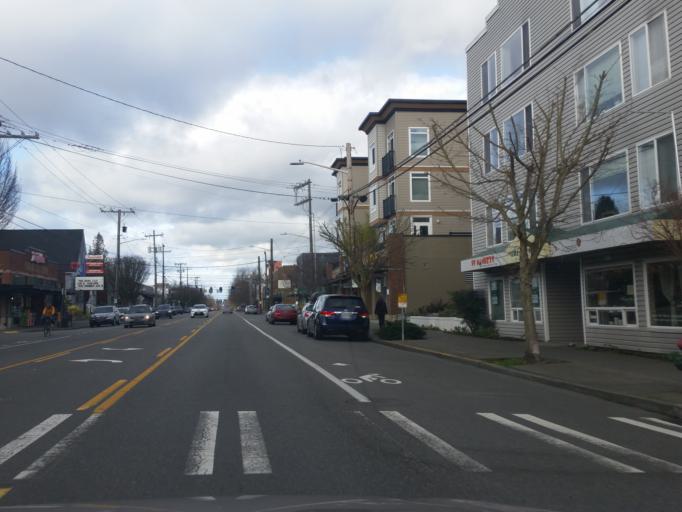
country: US
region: Washington
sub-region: King County
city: Shoreline
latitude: 47.6804
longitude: -122.3553
